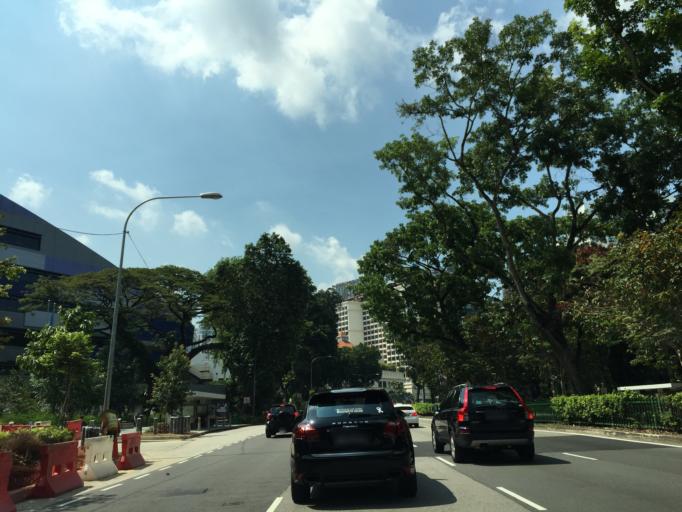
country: SG
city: Singapore
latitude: 1.3060
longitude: 103.8213
